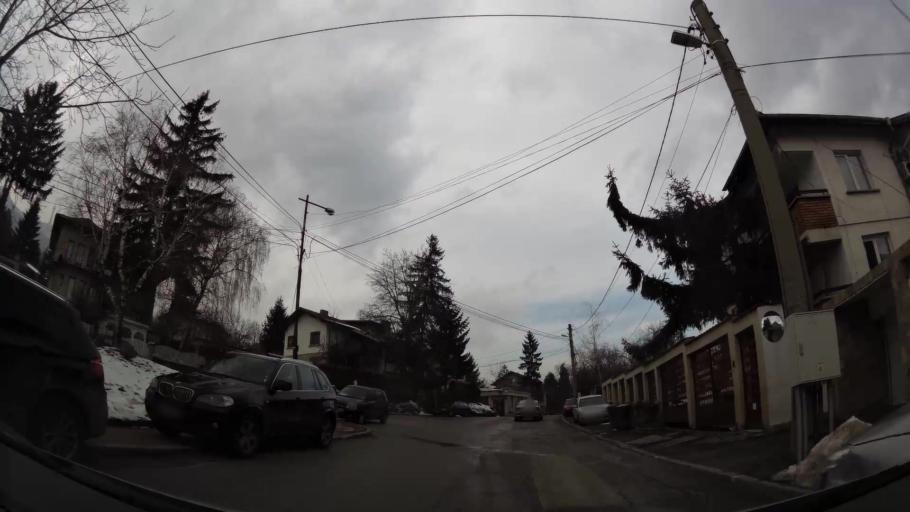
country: BG
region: Sofia-Capital
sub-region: Stolichna Obshtina
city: Sofia
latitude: 42.6489
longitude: 23.2624
